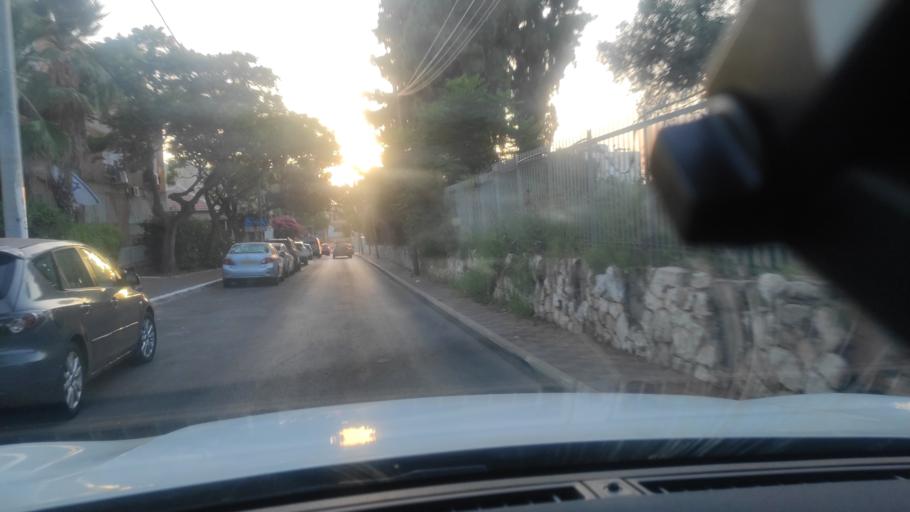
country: IL
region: Central District
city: Kfar Saba
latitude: 32.1832
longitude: 34.9057
